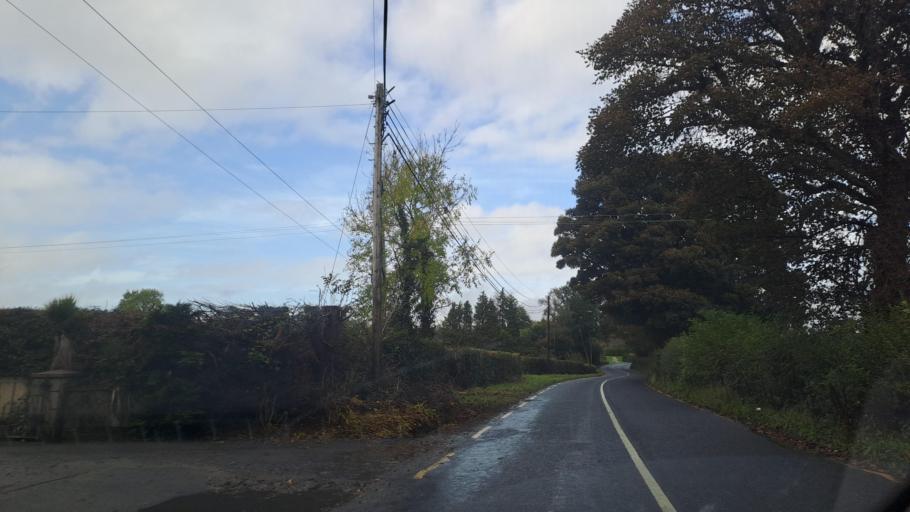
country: IE
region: Ulster
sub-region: County Monaghan
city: Carrickmacross
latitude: 53.9390
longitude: -6.7171
